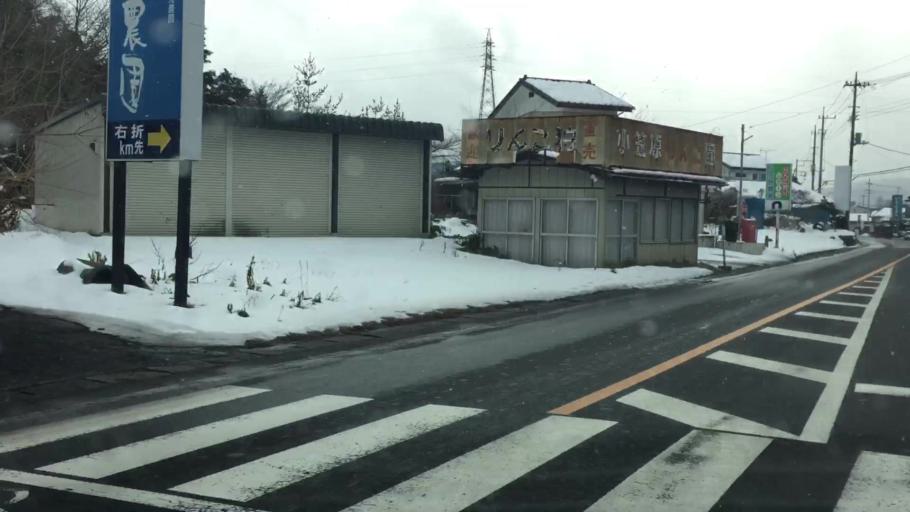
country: JP
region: Gunma
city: Numata
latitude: 36.6598
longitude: 139.0781
